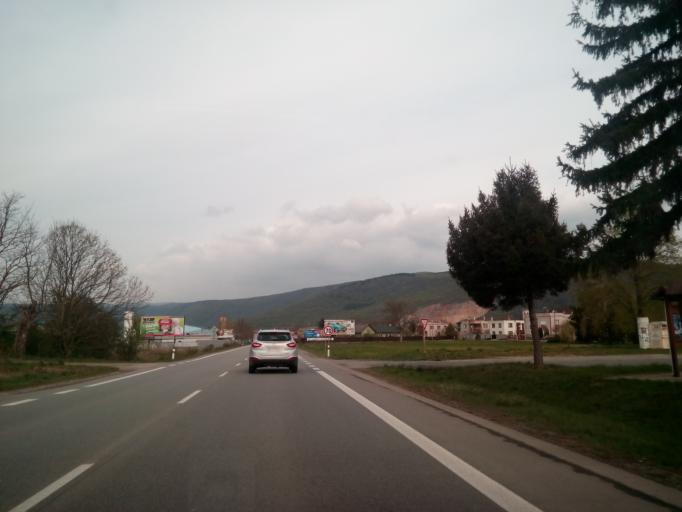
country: SK
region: Kosicky
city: Moldava nad Bodvou
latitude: 48.6074
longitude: 20.9504
